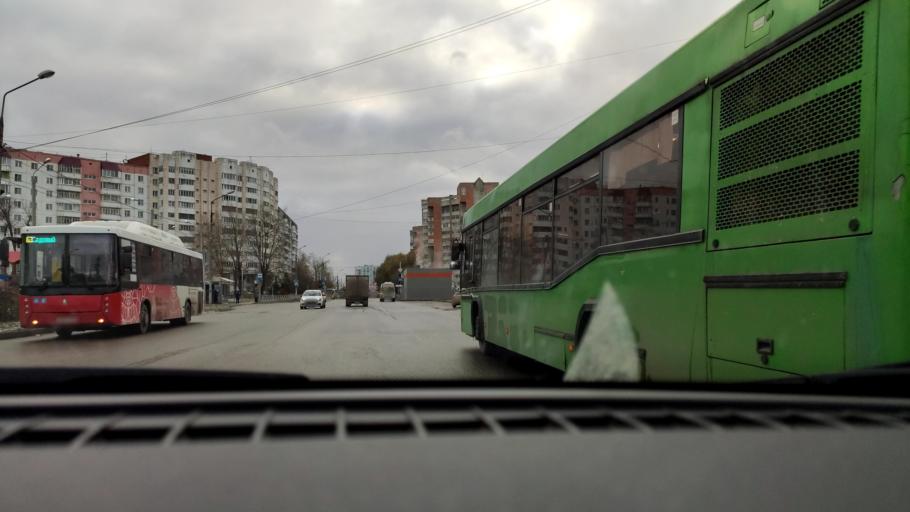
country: RU
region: Perm
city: Perm
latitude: 57.9707
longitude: 56.2299
